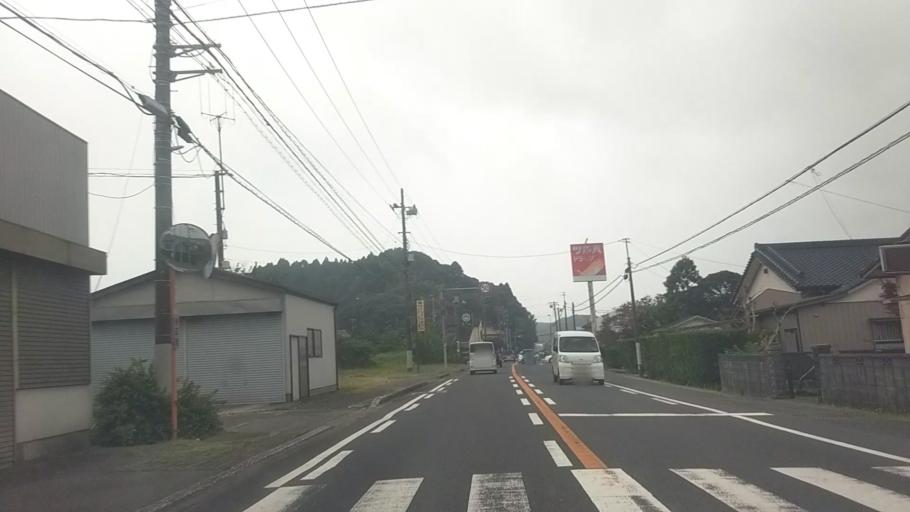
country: JP
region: Chiba
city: Ohara
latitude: 35.2305
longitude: 140.3878
